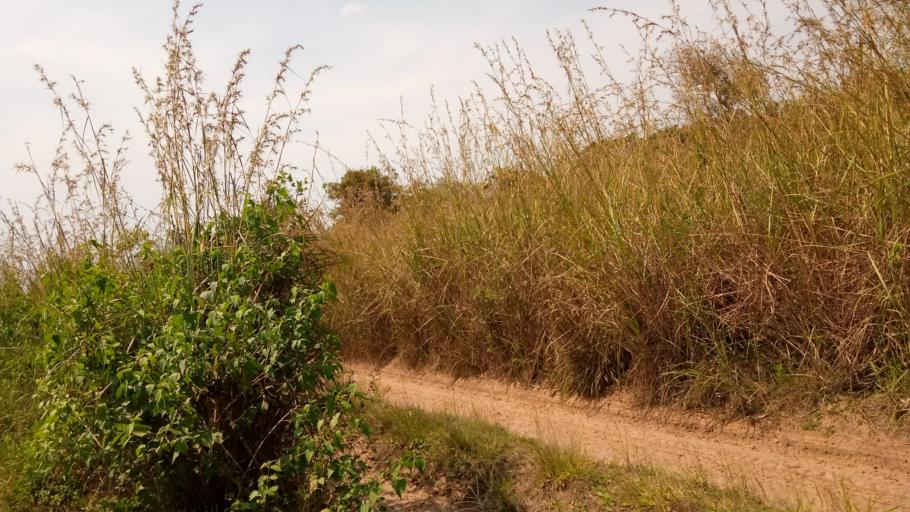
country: CD
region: Bandundu
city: Bandundu
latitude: -4.1713
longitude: 17.3959
